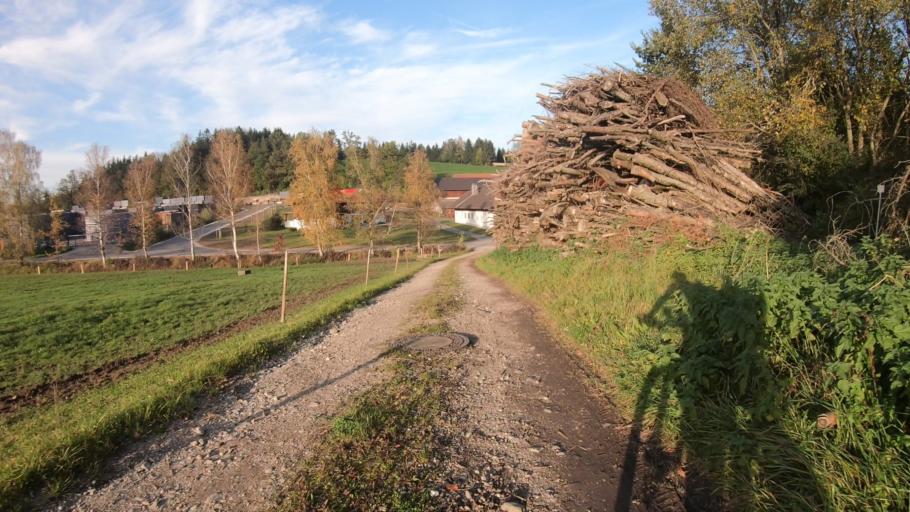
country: DE
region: Bavaria
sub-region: Upper Bavaria
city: Bergen
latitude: 47.8115
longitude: 12.6085
